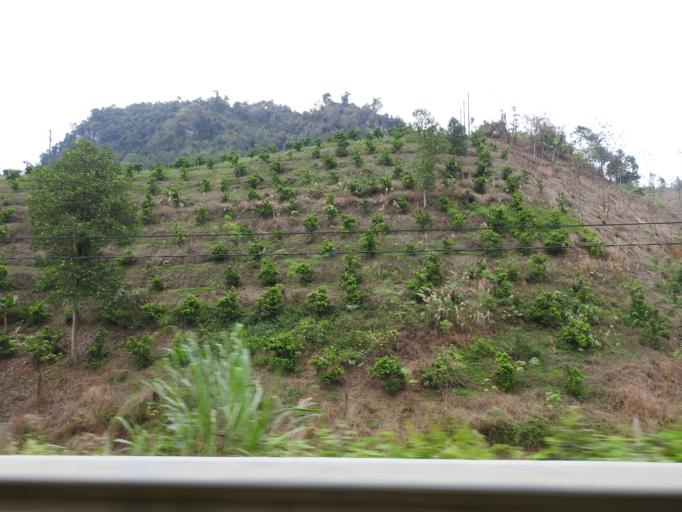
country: VN
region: Lao Cai
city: Thi Tran Pho Rang
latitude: 22.2981
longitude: 104.3600
